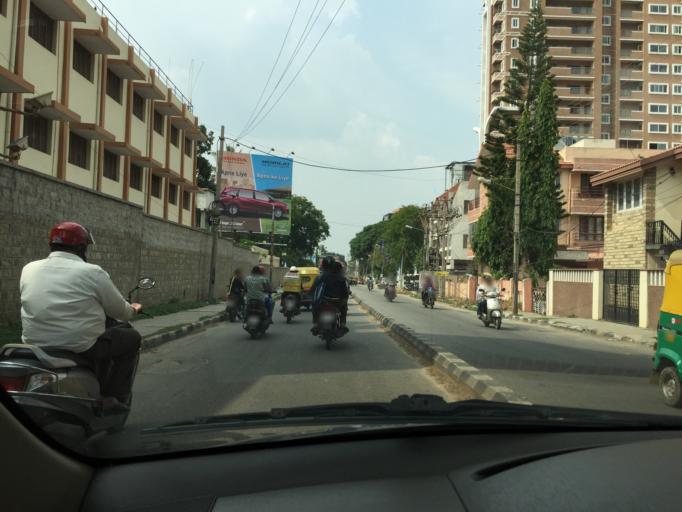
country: IN
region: Karnataka
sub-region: Bangalore Urban
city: Bangalore
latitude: 12.9919
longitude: 77.6146
